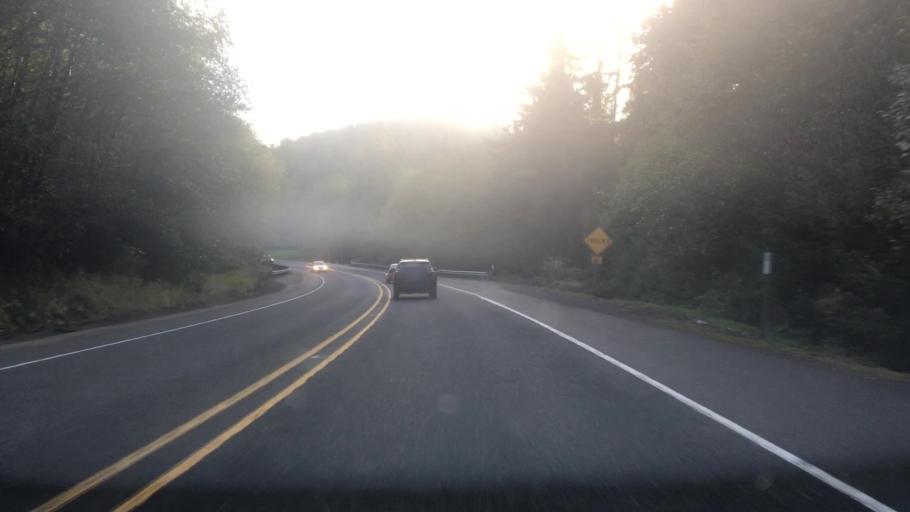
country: US
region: Oregon
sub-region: Clatsop County
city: Cannon Beach
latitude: 45.9348
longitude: -123.9262
